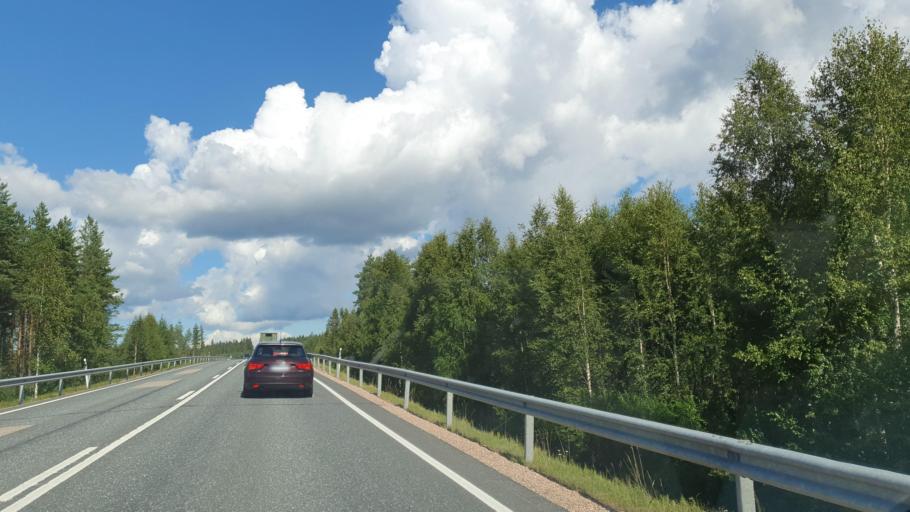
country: FI
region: Kainuu
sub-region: Kajaani
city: Kajaani
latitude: 64.0814
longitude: 27.4529
